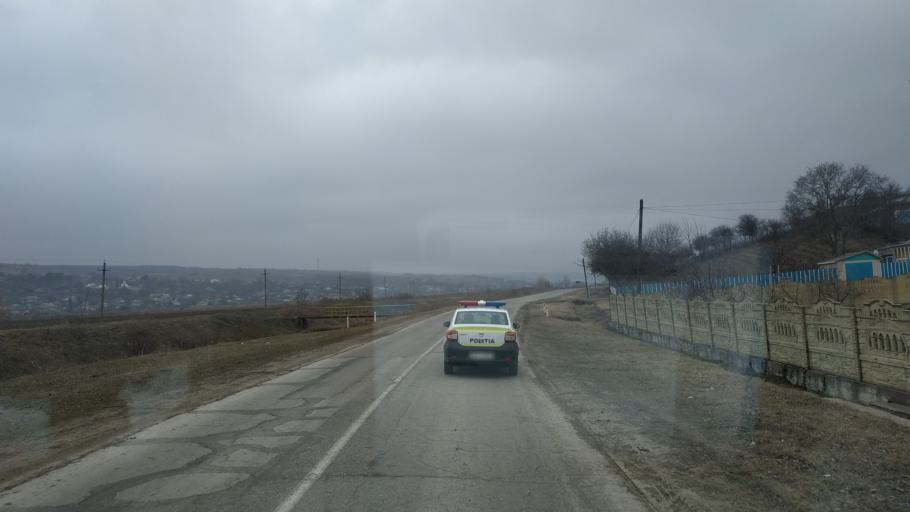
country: MD
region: Hincesti
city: Hincesti
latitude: 46.9763
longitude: 28.4688
